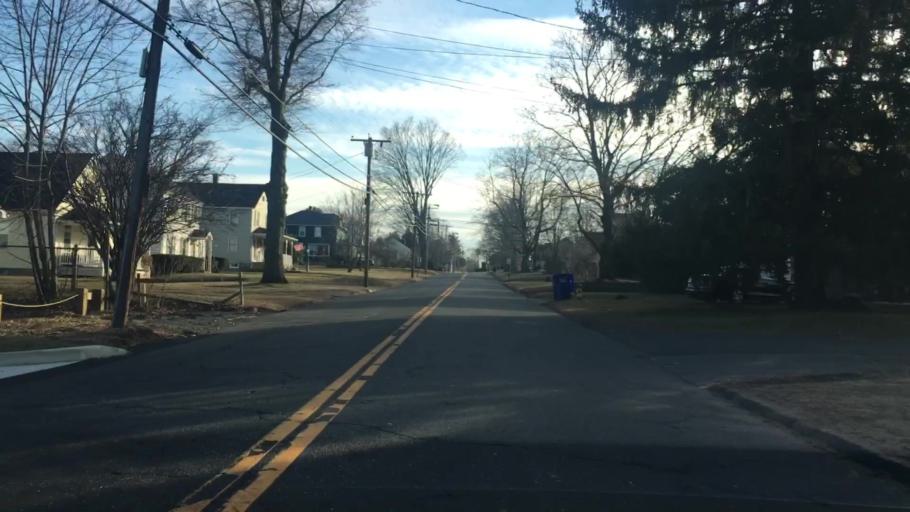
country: US
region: Connecticut
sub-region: Middlesex County
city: Middletown
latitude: 41.5391
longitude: -72.6501
